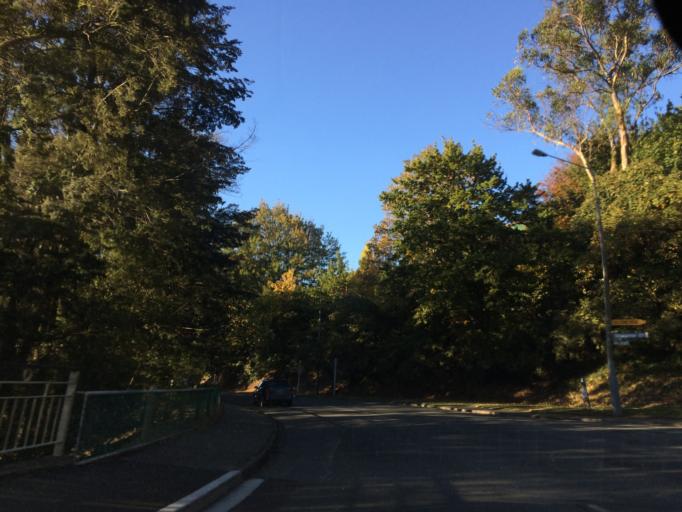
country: NZ
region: Canterbury
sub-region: Christchurch City
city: Christchurch
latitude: -43.5738
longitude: 172.6170
